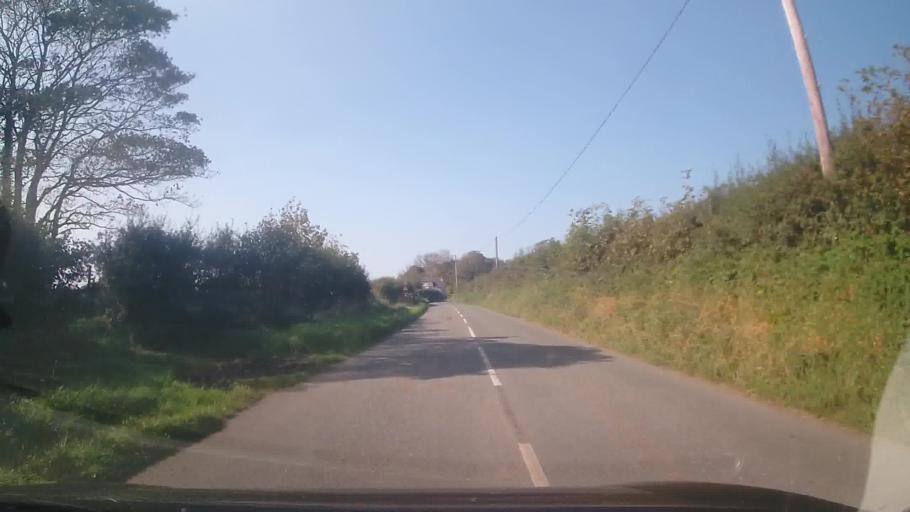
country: GB
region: Wales
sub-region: Pembrokeshire
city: Camrose
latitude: 51.8415
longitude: -4.9954
